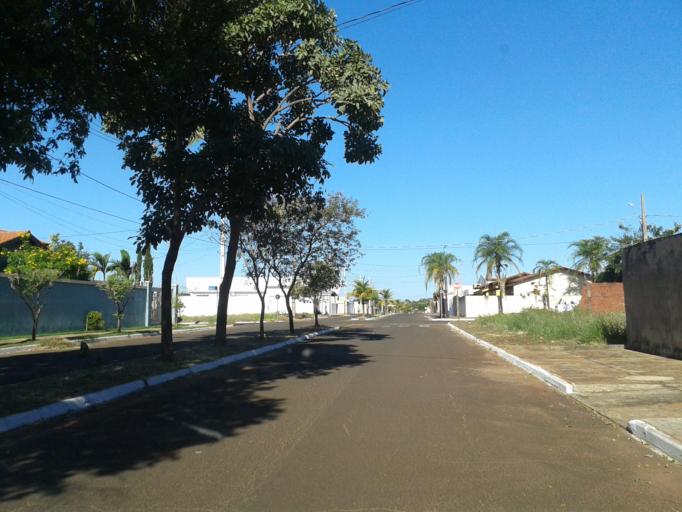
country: BR
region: Minas Gerais
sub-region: Santa Vitoria
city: Santa Vitoria
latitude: -18.8497
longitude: -50.1238
